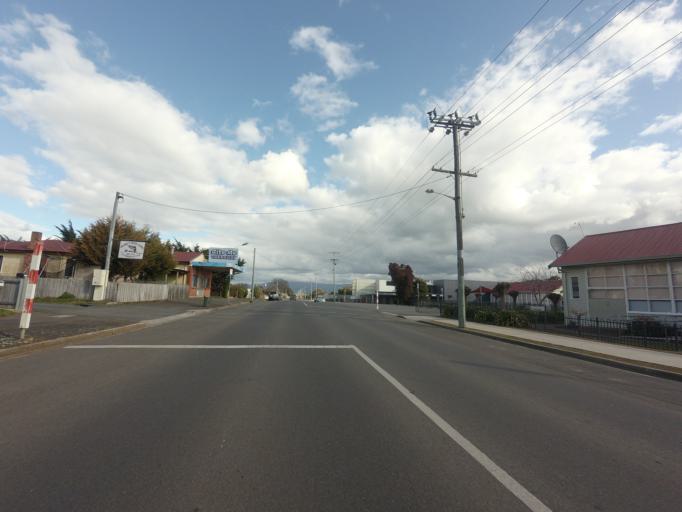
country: AU
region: Tasmania
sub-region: Northern Midlands
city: Longford
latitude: -41.6907
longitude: 147.0793
